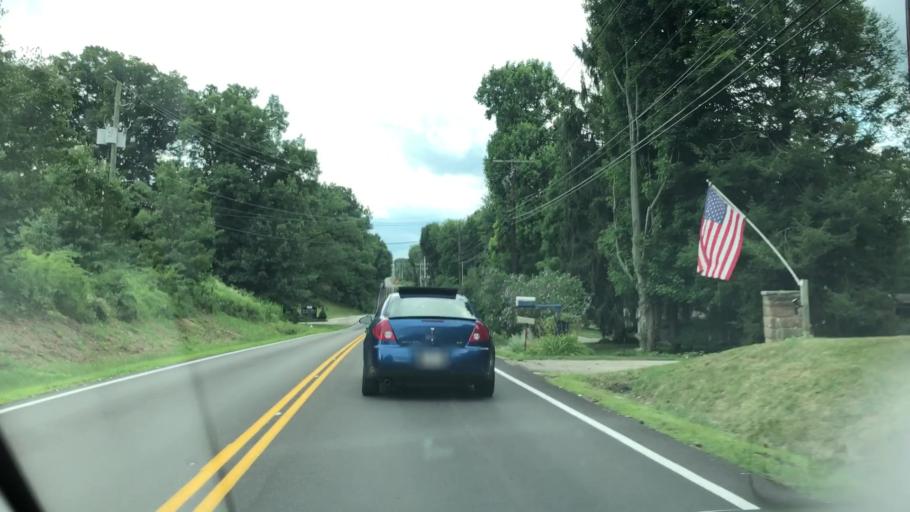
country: US
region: Ohio
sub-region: Summit County
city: Greensburg
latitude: 40.8968
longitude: -81.4404
